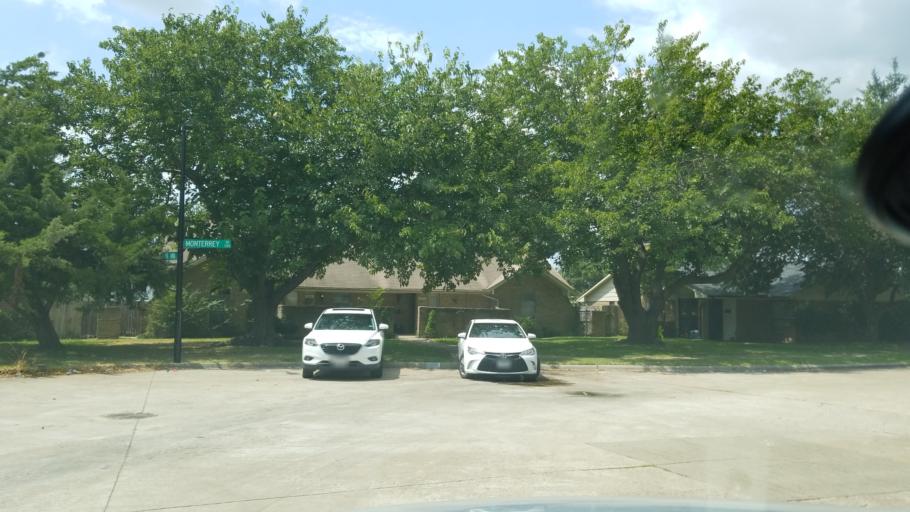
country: US
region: Texas
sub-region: Dallas County
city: Garland
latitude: 32.9243
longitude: -96.6583
